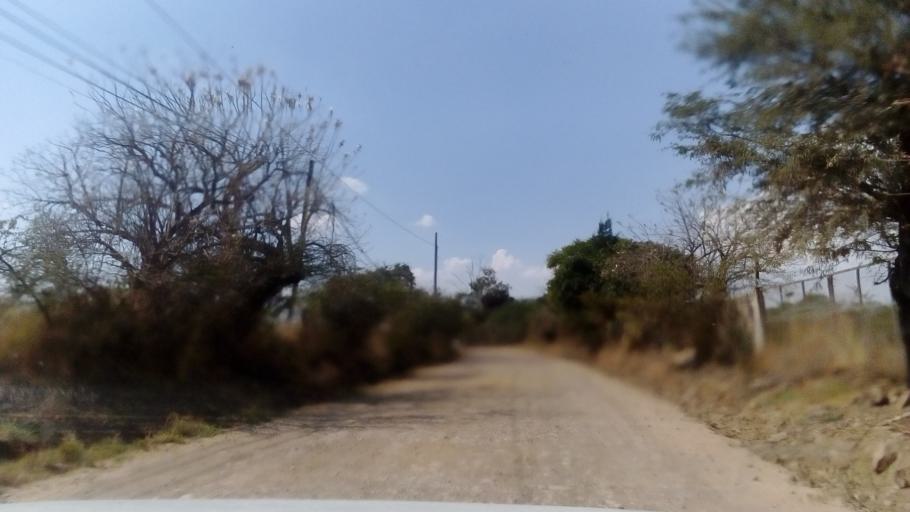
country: MX
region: Guanajuato
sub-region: Silao de la Victoria
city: San Francisco (Banos de Agua Caliente)
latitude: 21.0761
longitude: -101.4892
